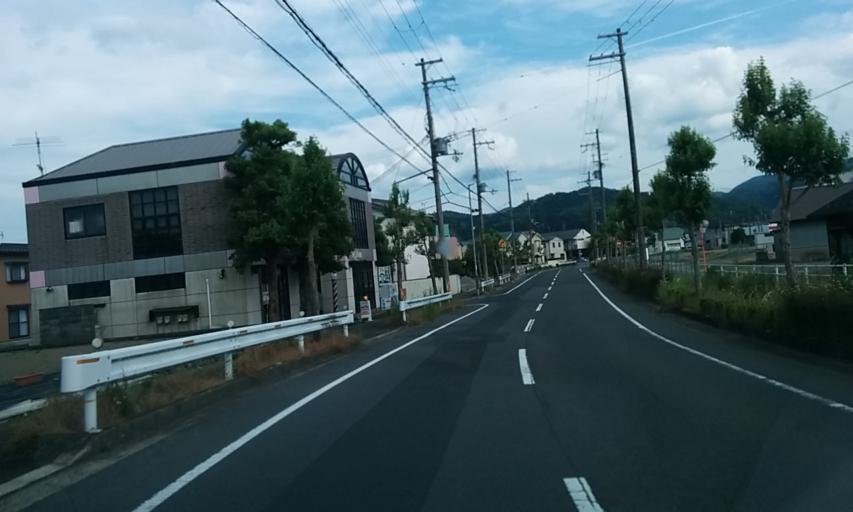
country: JP
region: Kyoto
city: Ayabe
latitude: 35.3074
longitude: 135.2612
